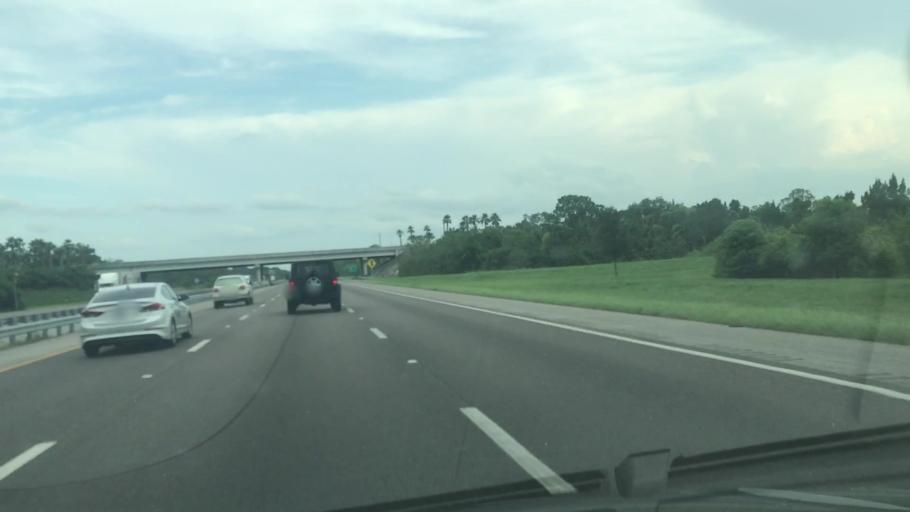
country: US
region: Florida
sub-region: Brevard County
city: Port Saint John
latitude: 28.5028
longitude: -80.8406
